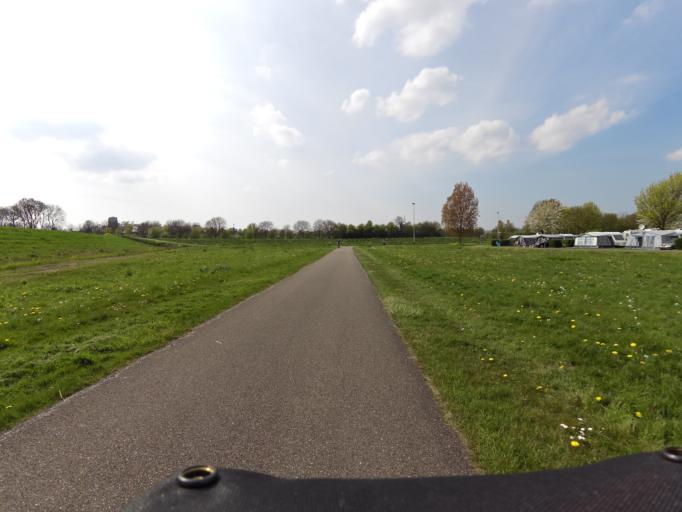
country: NL
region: South Holland
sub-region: Gemeente Brielle
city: Brielle
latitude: 51.9043
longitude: 4.1747
